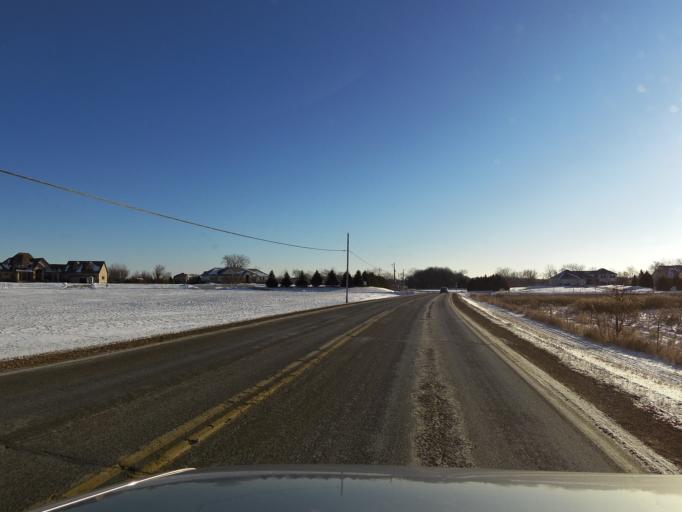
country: US
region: Minnesota
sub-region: Scott County
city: Shakopee
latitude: 44.7329
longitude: -93.5327
